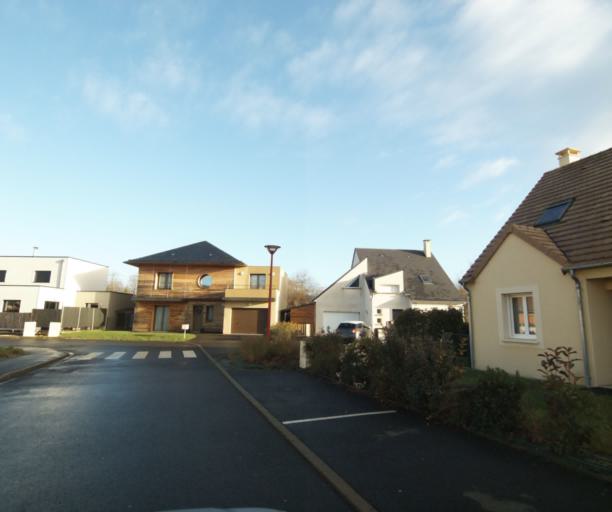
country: FR
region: Pays de la Loire
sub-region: Departement de la Sarthe
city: Sarge-les-le-Mans
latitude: 48.0178
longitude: 0.2358
